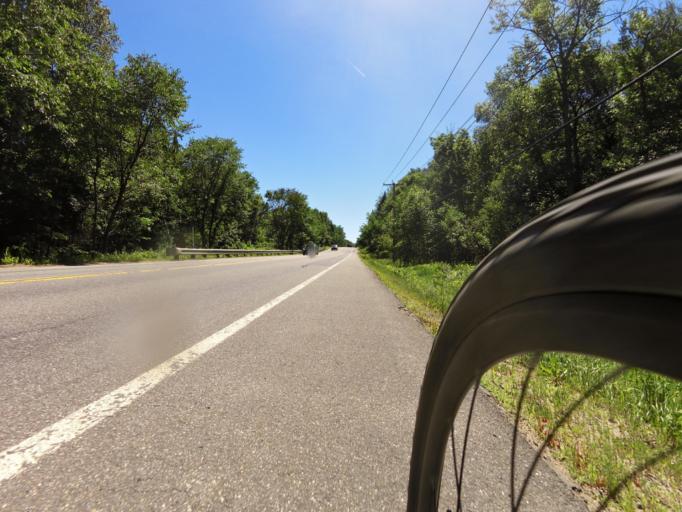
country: CA
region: Quebec
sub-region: Laurentides
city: Mont-Tremblant
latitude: 46.0993
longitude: -74.6185
